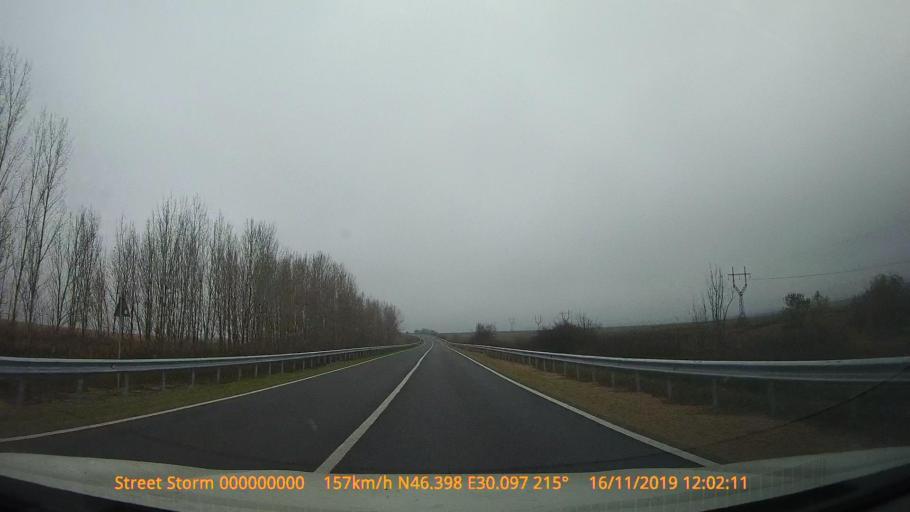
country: UA
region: Odessa
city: Starokozache
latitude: 46.3967
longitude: 30.0951
